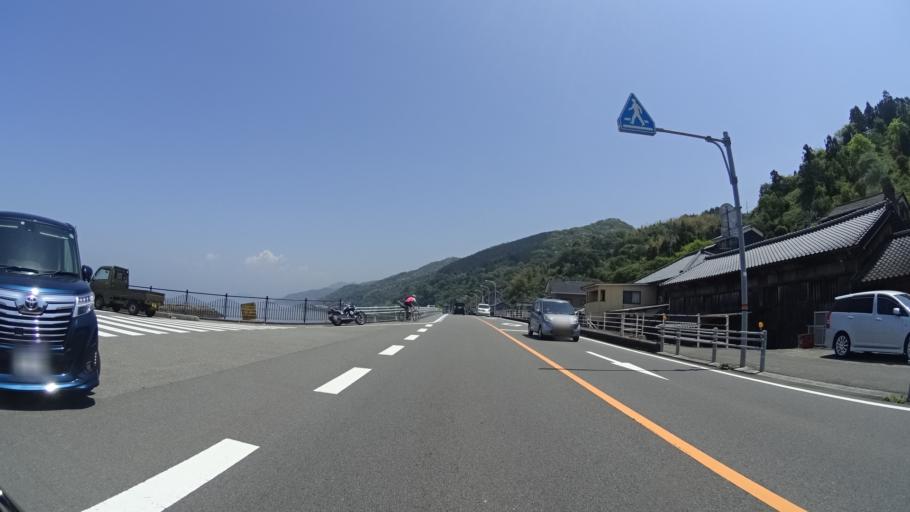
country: JP
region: Ehime
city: Ozu
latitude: 33.6521
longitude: 132.5811
